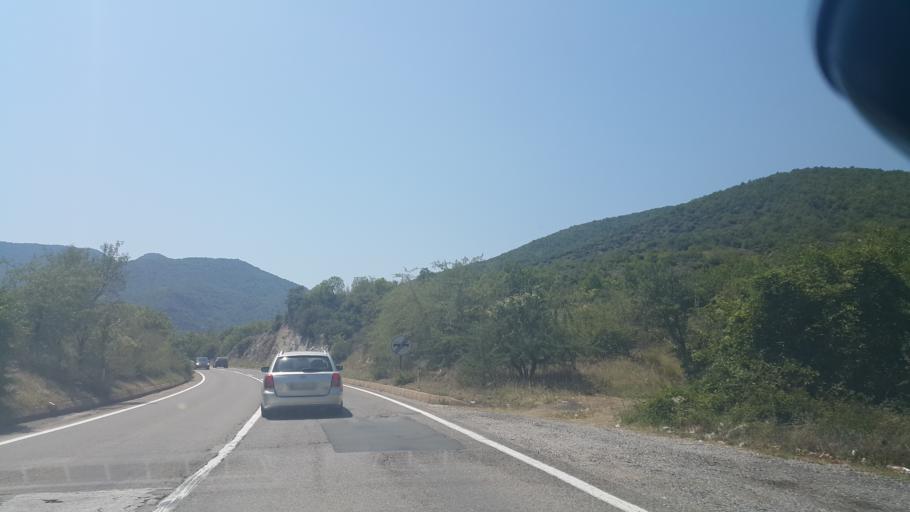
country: MK
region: Gevgelija
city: Miravci
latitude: 41.3792
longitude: 22.3998
